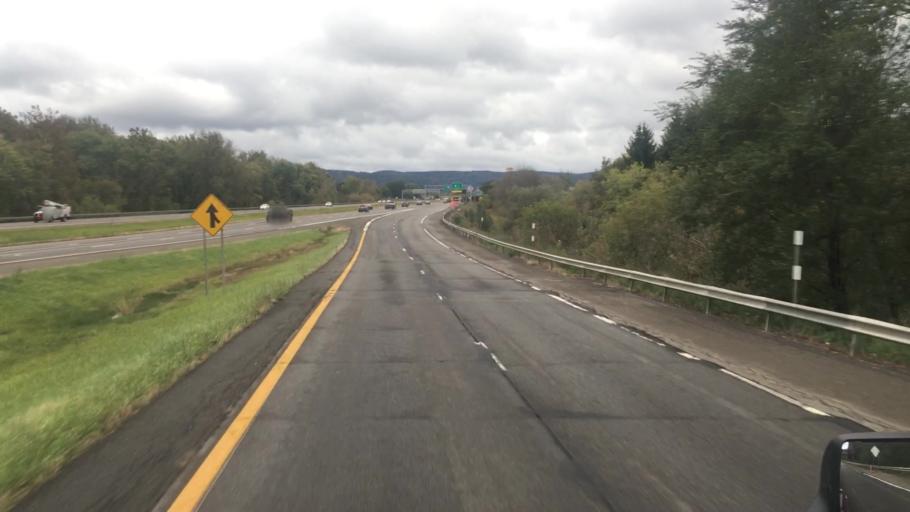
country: US
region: New York
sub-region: Broome County
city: Port Dickinson
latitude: 42.1388
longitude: -75.9029
